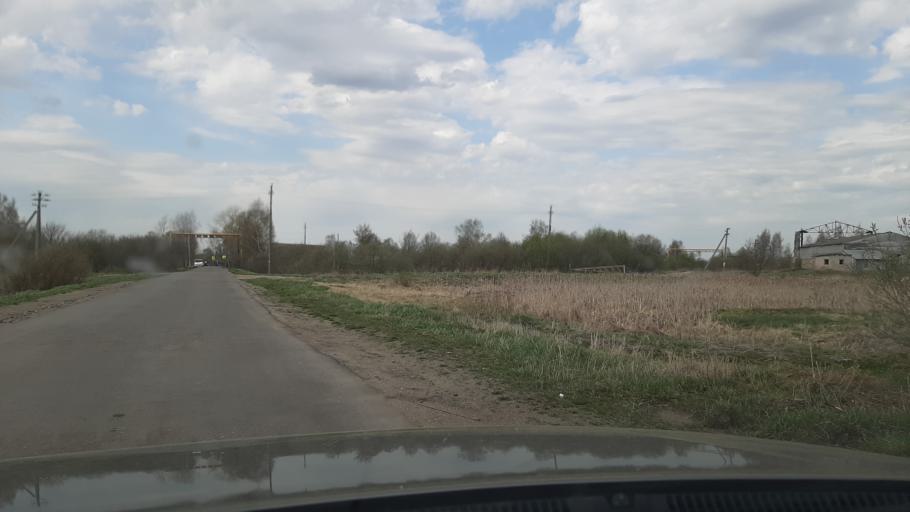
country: RU
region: Ivanovo
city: Privolzhsk
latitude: 57.3277
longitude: 41.2363
